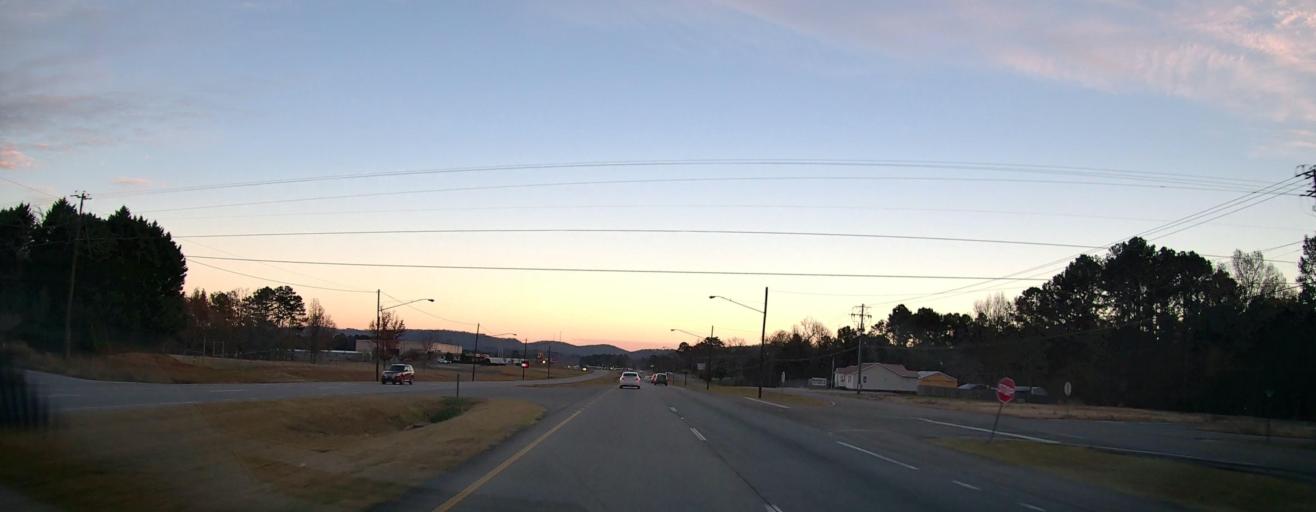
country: US
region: Alabama
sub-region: Etowah County
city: Glencoe
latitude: 33.9725
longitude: -85.9500
